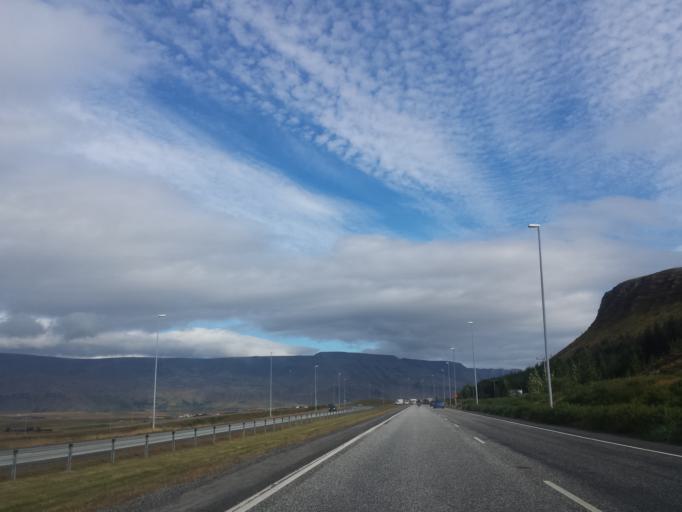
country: IS
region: Capital Region
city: Mosfellsbaer
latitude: 64.1506
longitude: -21.7413
